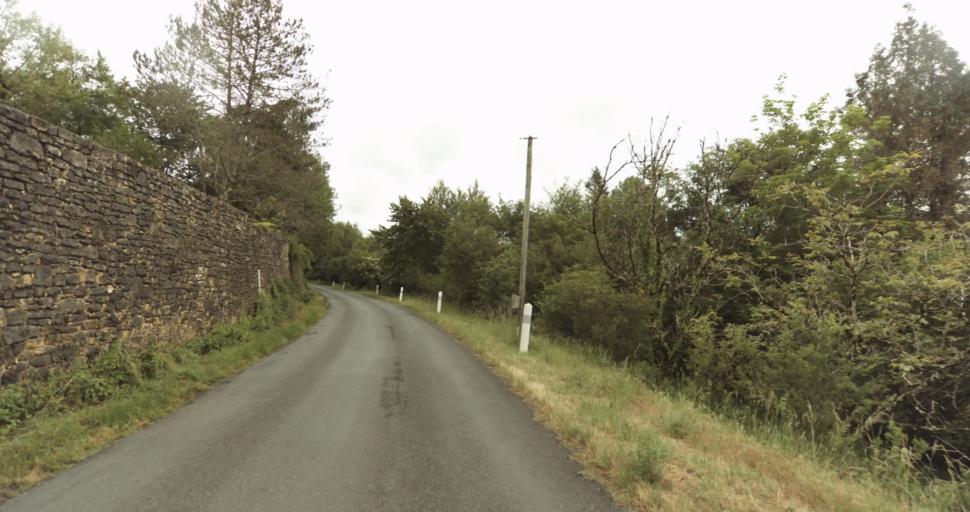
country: FR
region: Aquitaine
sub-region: Departement de la Dordogne
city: Beaumont-du-Perigord
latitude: 44.7645
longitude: 0.8049
